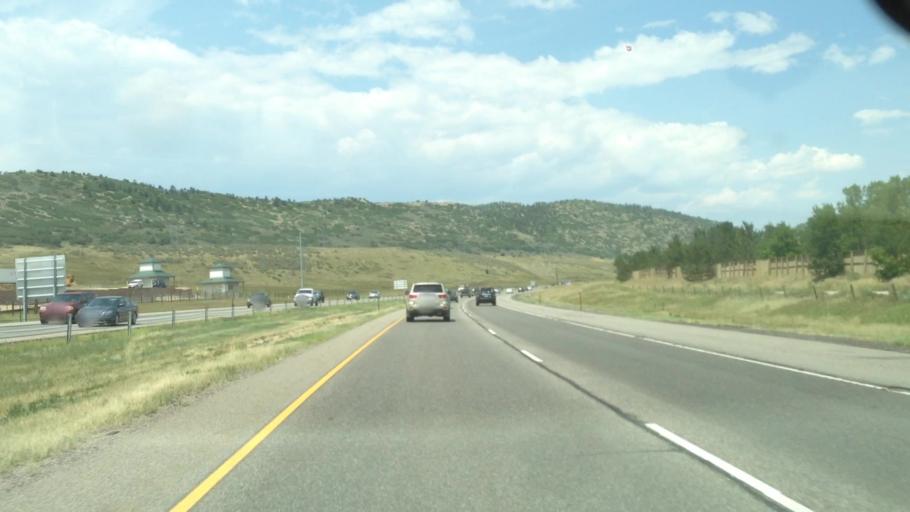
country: US
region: Colorado
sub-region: Jefferson County
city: Ken Caryl
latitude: 39.5614
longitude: -105.1212
